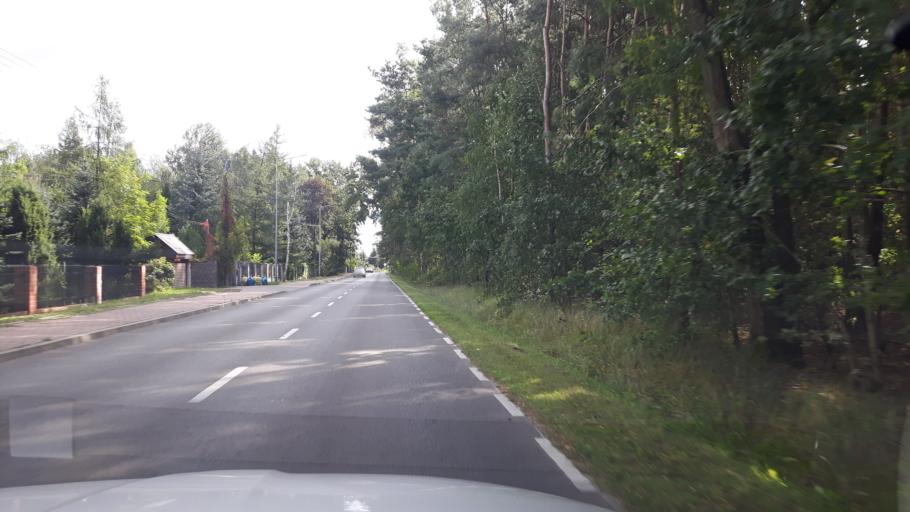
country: PL
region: Masovian Voivodeship
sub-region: Powiat legionowski
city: Stanislawow Pierwszy
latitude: 52.3958
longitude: 21.0534
